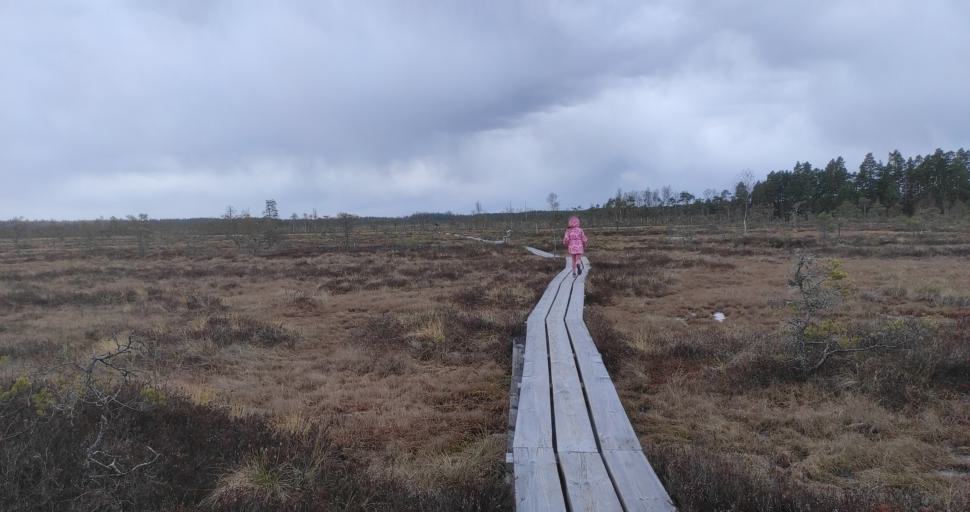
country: LV
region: Dundaga
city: Dundaga
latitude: 57.3462
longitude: 22.1567
